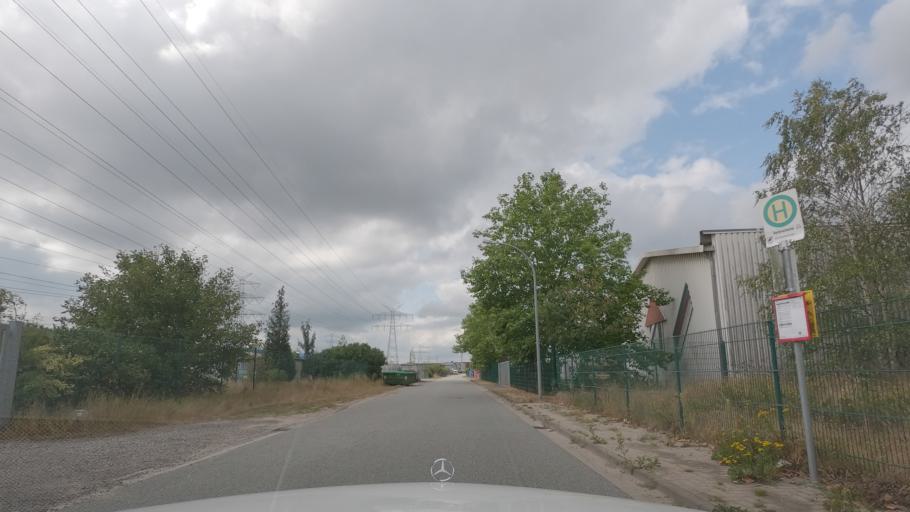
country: DE
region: Lower Saxony
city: Neuenkirchen
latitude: 53.2278
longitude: 8.5371
